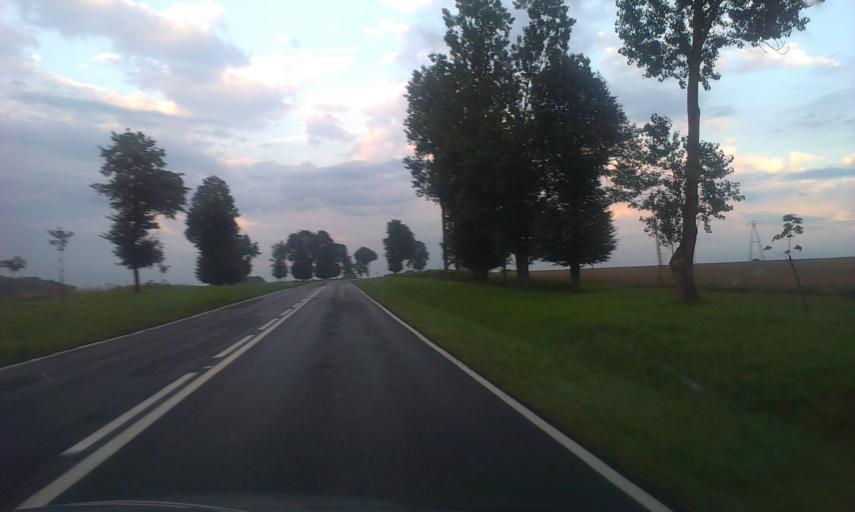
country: PL
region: West Pomeranian Voivodeship
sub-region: Powiat koszalinski
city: Sianow
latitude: 54.1393
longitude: 16.2730
